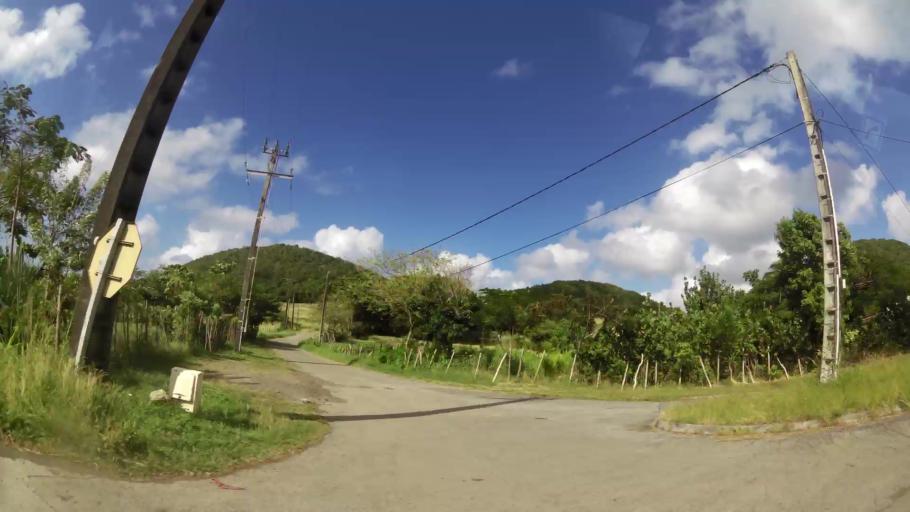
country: MQ
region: Martinique
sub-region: Martinique
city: Le Marin
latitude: 14.4190
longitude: -60.8777
